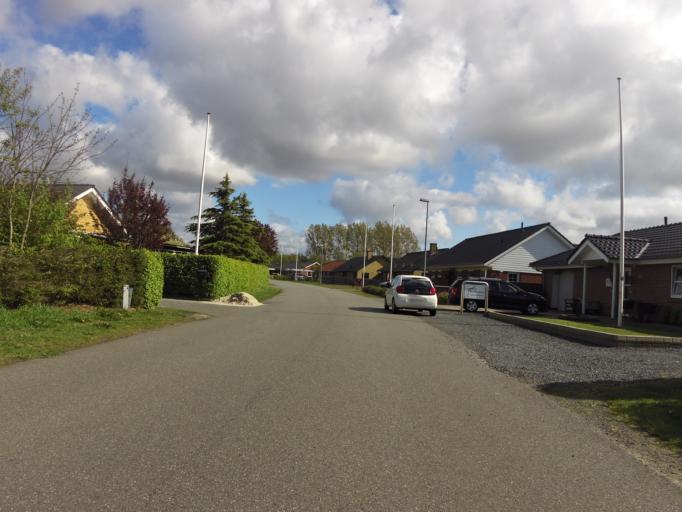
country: DK
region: South Denmark
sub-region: Esbjerg Kommune
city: Ribe
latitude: 55.2759
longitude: 8.7224
